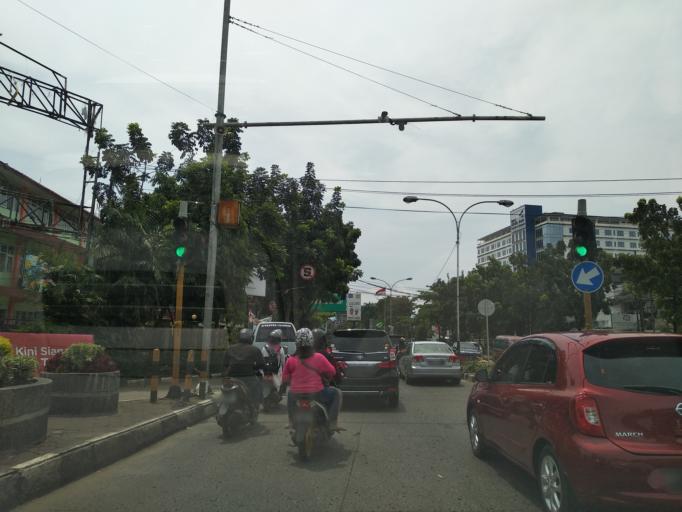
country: ID
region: West Java
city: Bandung
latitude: -6.9369
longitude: 107.6227
